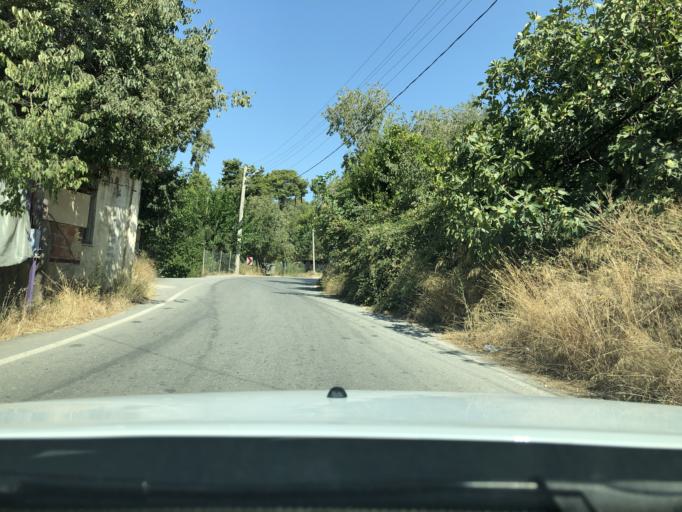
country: TR
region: Antalya
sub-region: Manavgat
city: Manavgat
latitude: 36.8131
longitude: 31.4887
